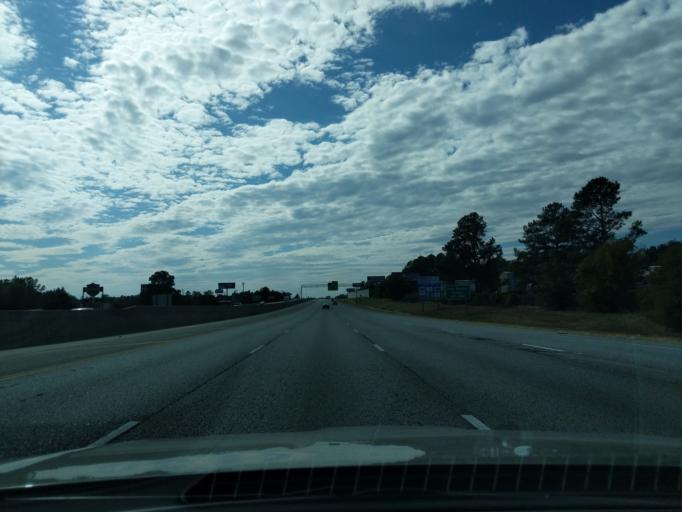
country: US
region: Georgia
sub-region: Columbia County
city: Evans
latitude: 33.4863
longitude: -82.1149
